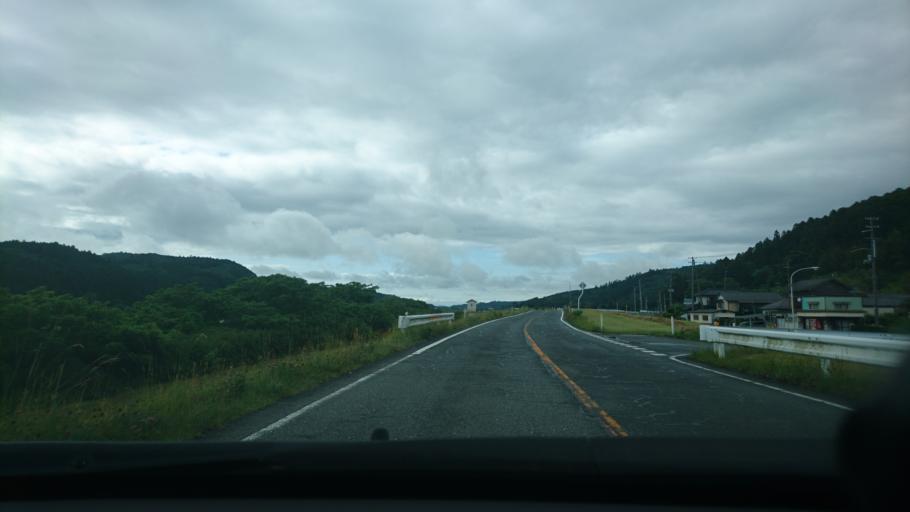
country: JP
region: Miyagi
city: Wakuya
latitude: 38.6225
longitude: 141.2959
